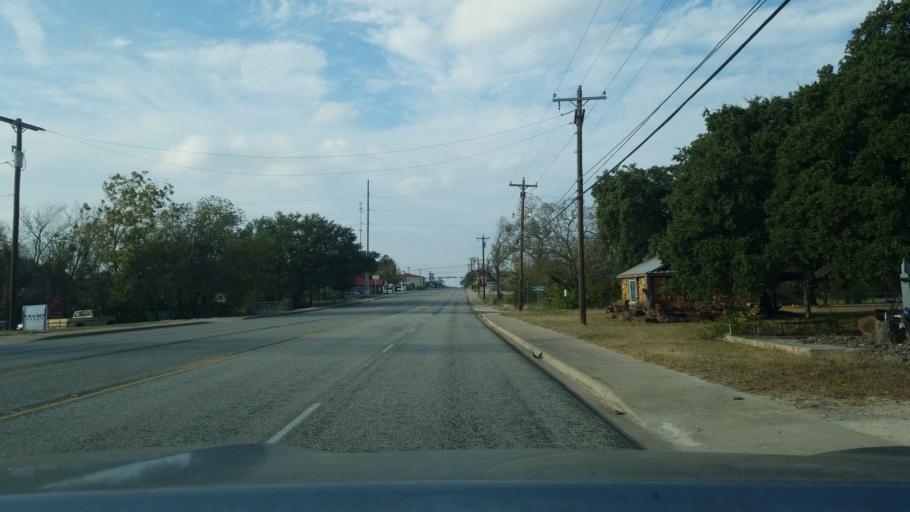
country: US
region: Texas
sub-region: Lampasas County
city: Lampasas
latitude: 31.2133
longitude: -98.3919
